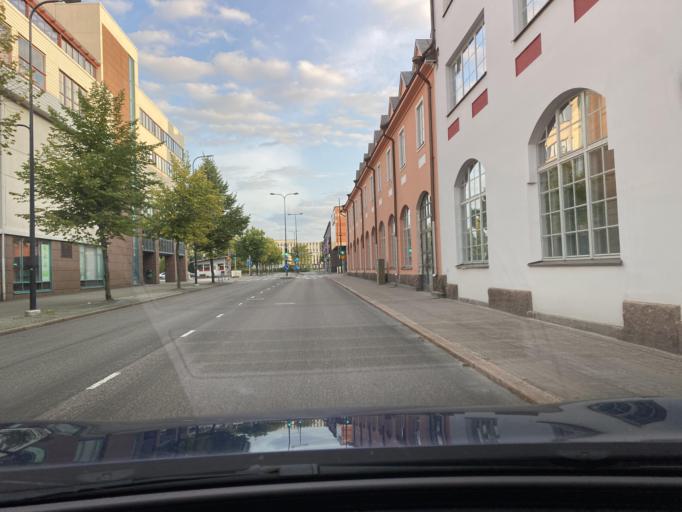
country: FI
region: Kymenlaakso
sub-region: Kouvola
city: Kouvola
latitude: 60.8689
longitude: 26.7080
